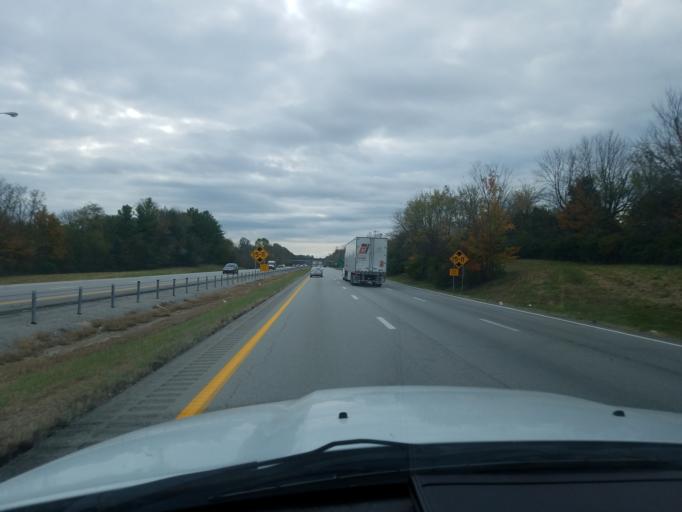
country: US
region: Kentucky
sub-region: Jefferson County
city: Middletown
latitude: 38.2179
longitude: -85.5063
